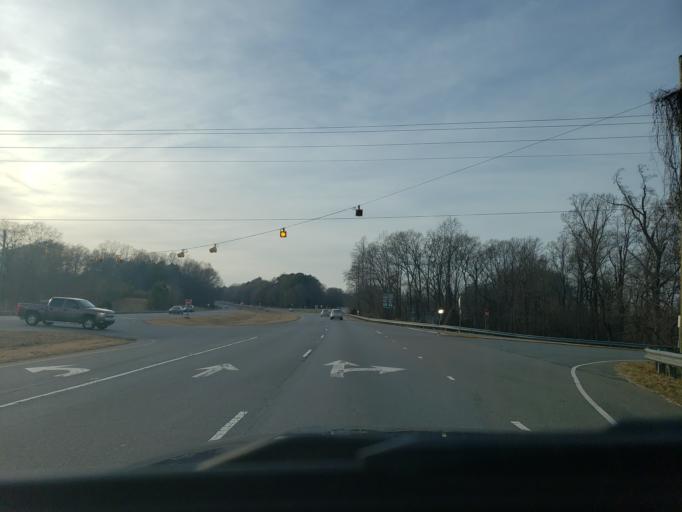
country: US
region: North Carolina
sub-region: Cleveland County
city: Boiling Springs
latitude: 35.3025
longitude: -81.6950
